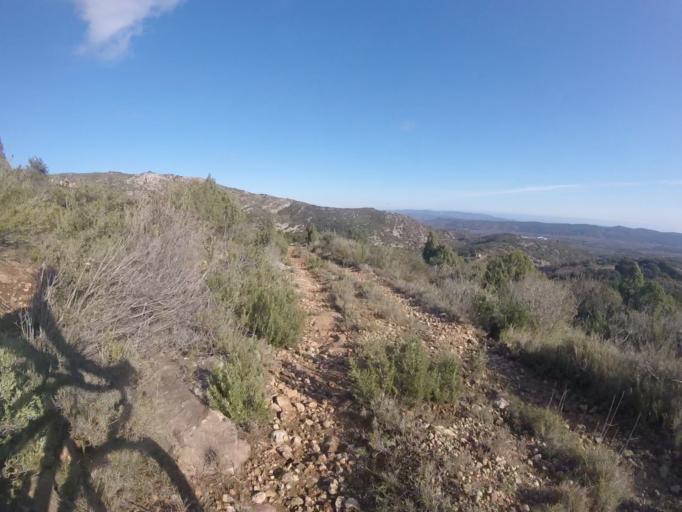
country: ES
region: Valencia
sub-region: Provincia de Castello
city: Sarratella
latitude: 40.2967
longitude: 0.0469
